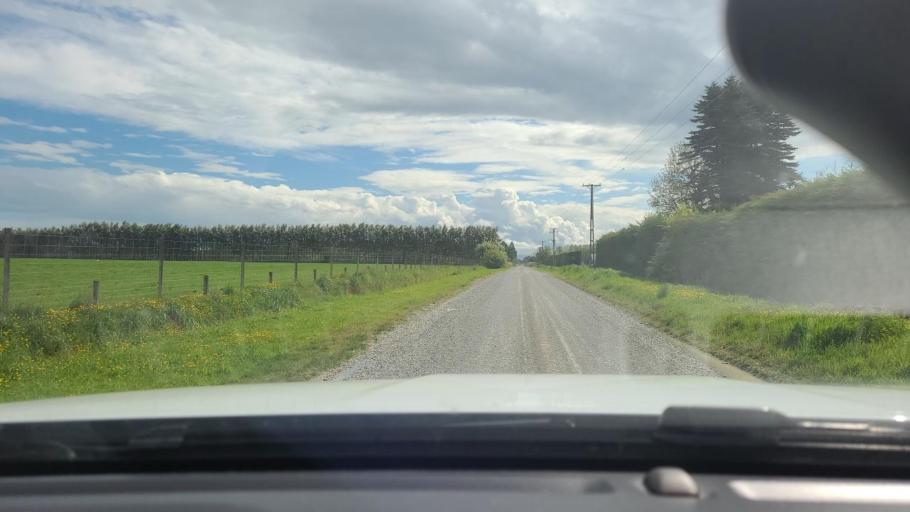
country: NZ
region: Southland
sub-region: Southland District
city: Winton
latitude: -46.1251
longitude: 168.3428
